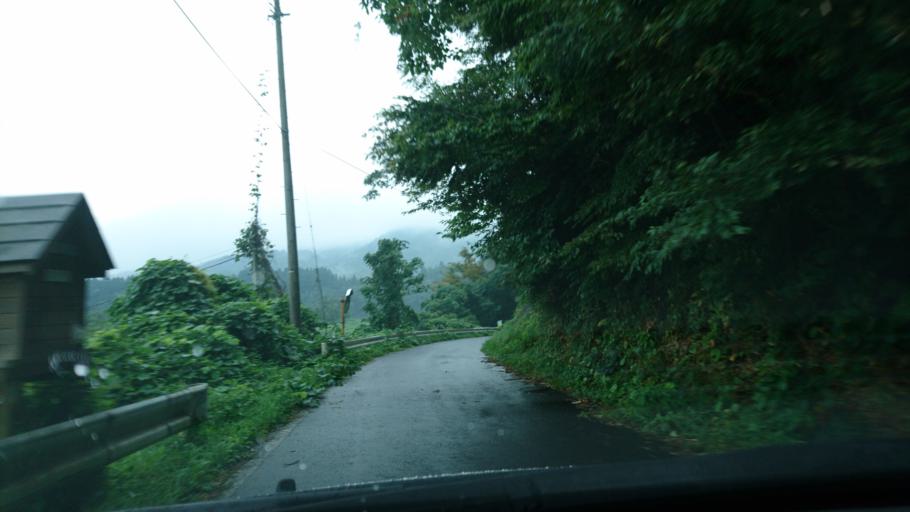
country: JP
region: Iwate
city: Ichinoseki
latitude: 38.8792
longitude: 141.2573
